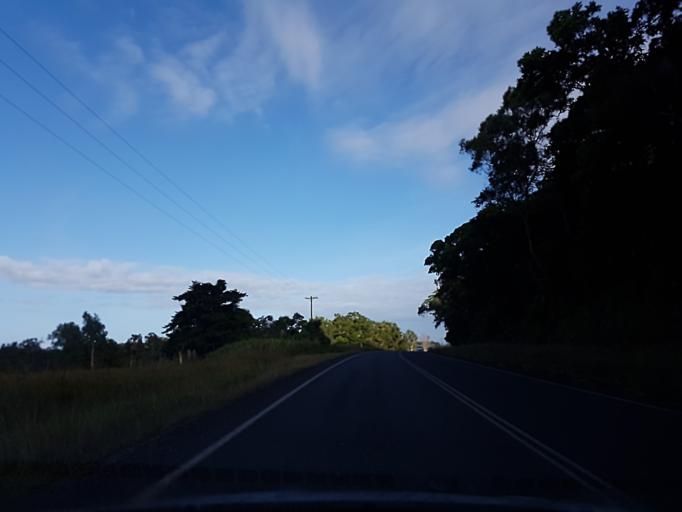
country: AU
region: Queensland
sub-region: Cairns
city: Port Douglas
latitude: -16.3222
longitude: 145.4076
